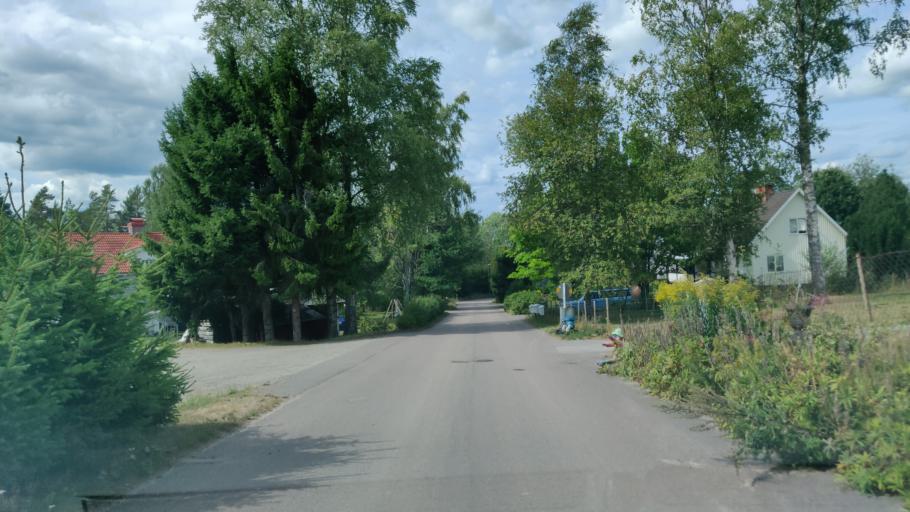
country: SE
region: Vaermland
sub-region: Hagfors Kommun
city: Hagfors
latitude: 60.0210
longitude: 13.6989
